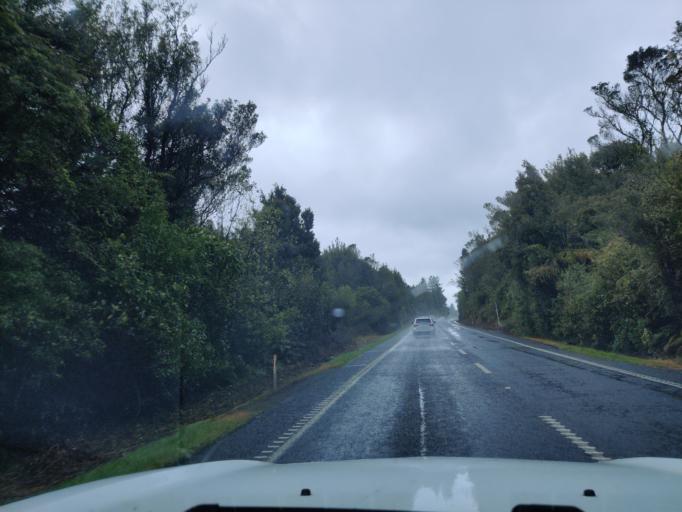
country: NZ
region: Bay of Plenty
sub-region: Rotorua District
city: Rotorua
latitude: -38.0578
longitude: 176.0904
